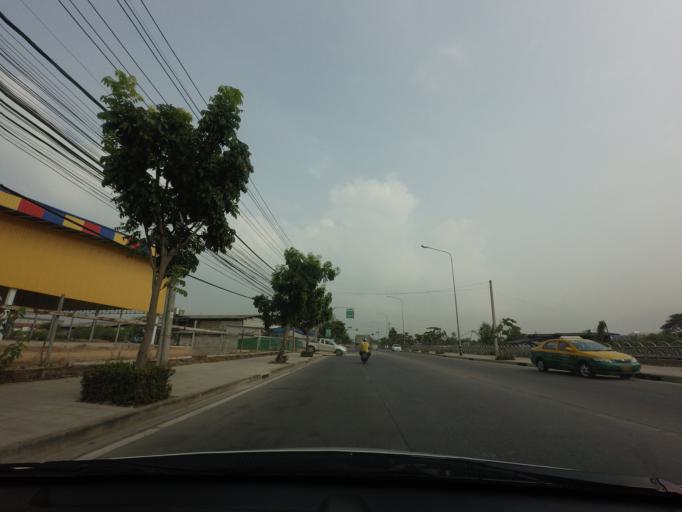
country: TH
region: Bangkok
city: Nong Khaem
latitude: 13.7424
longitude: 100.3568
